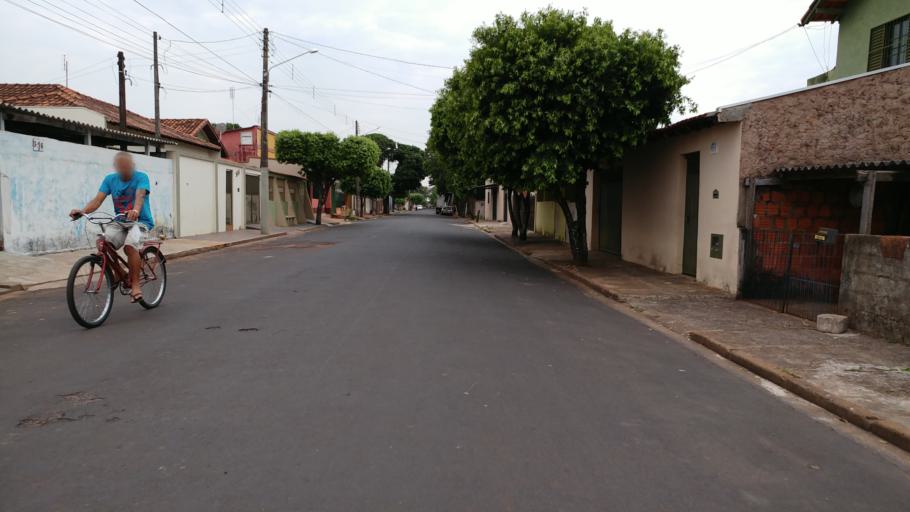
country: BR
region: Sao Paulo
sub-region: Paraguacu Paulista
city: Paraguacu Paulista
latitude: -22.4161
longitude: -50.5707
